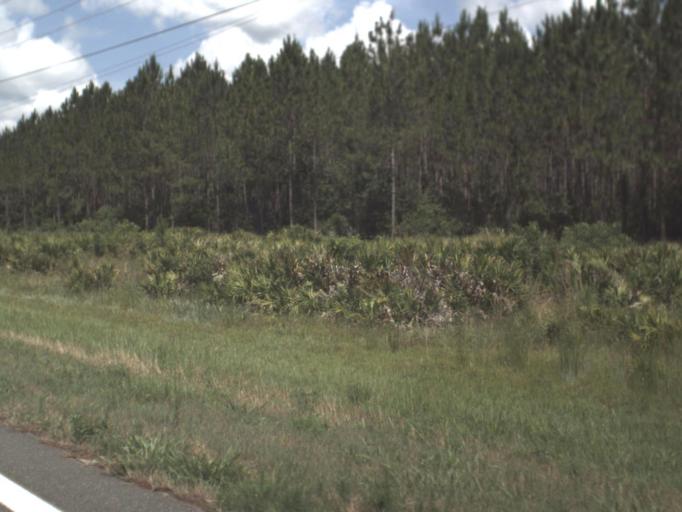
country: US
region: Florida
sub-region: Levy County
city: Chiefland
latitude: 29.2494
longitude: -82.9083
